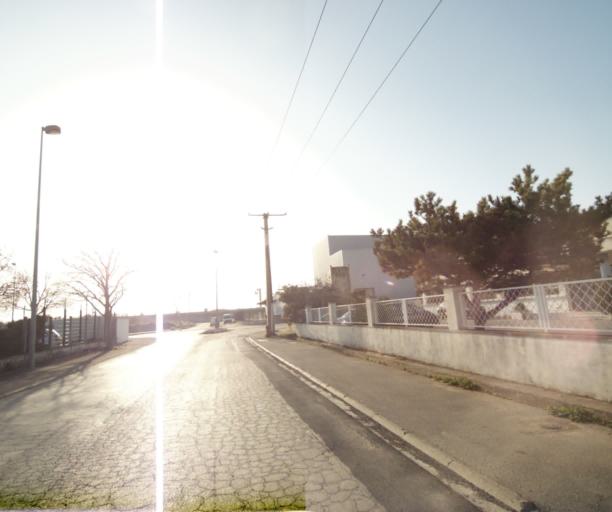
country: FR
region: Provence-Alpes-Cote d'Azur
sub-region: Departement des Bouches-du-Rhone
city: Saint-Victoret
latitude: 43.4237
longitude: 5.2516
